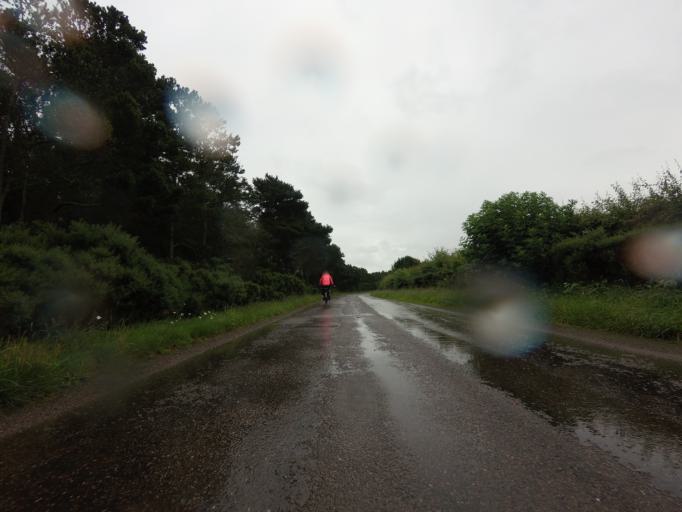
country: GB
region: Scotland
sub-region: Moray
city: Fochabers
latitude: 57.6648
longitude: -3.0740
